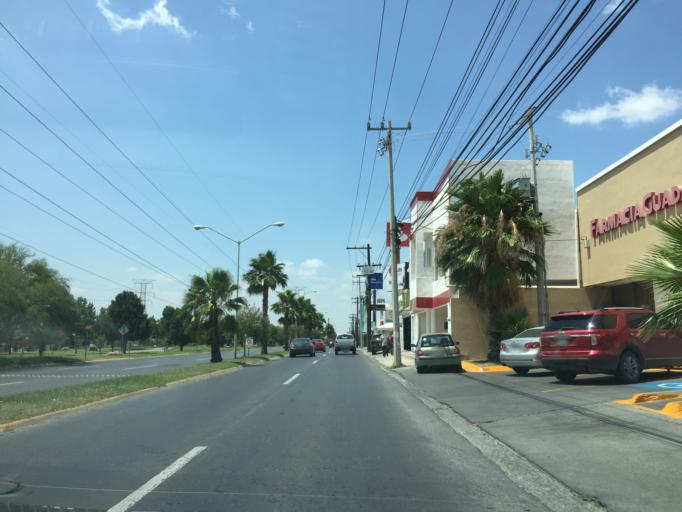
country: MX
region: Nuevo Leon
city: Guadalupe
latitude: 25.6427
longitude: -100.2685
